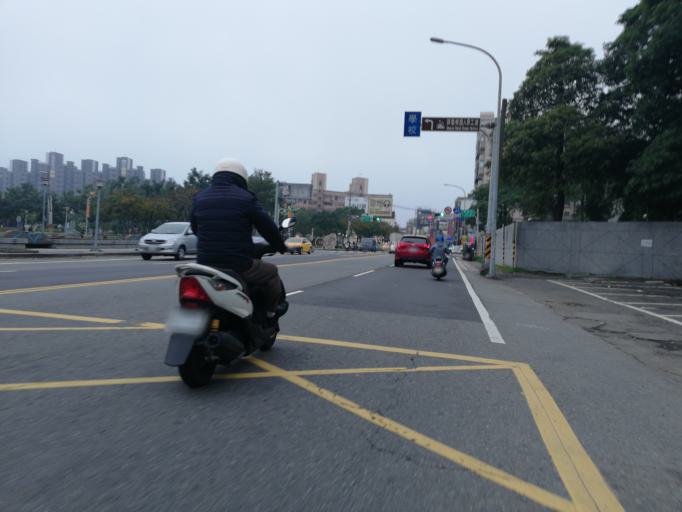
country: TW
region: Taiwan
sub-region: Taoyuan
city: Taoyuan
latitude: 24.9807
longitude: 121.3059
